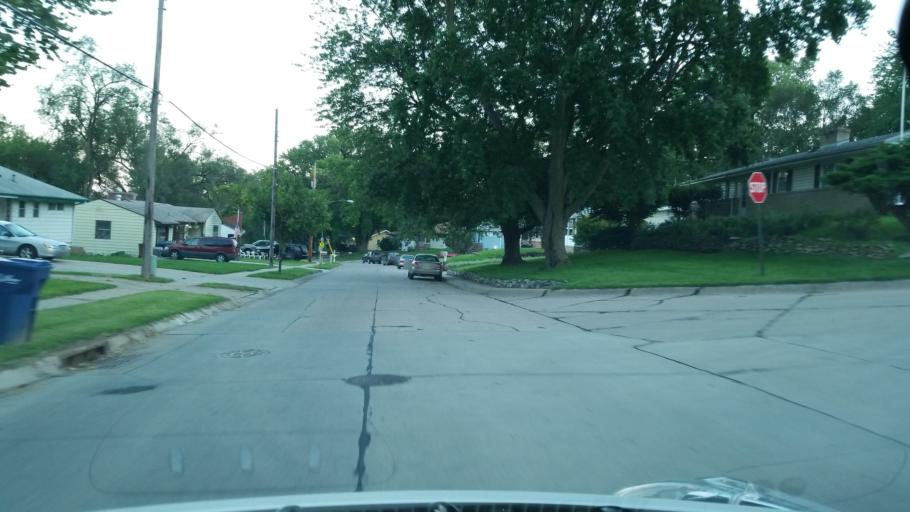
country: US
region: Nebraska
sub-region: Sarpy County
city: Bellevue
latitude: 41.1410
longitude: -95.9010
